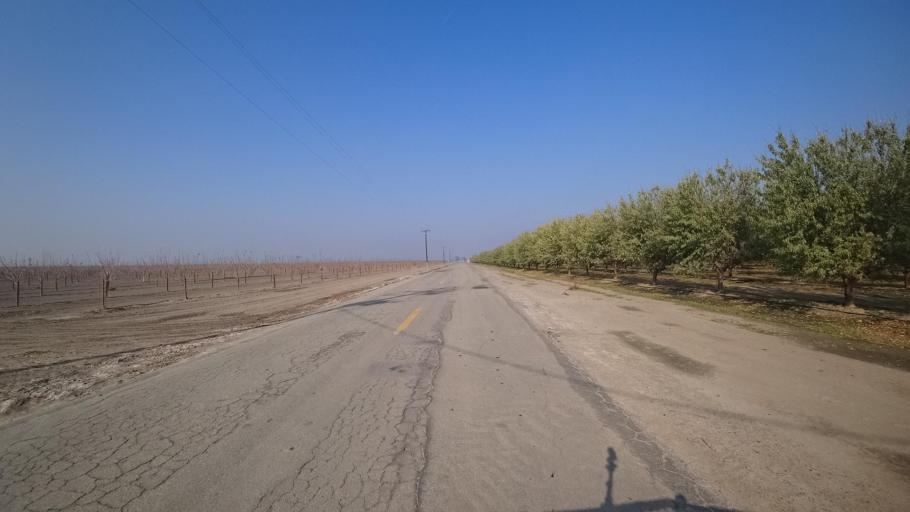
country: US
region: California
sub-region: Kern County
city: Greenfield
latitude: 35.1758
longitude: -119.0394
